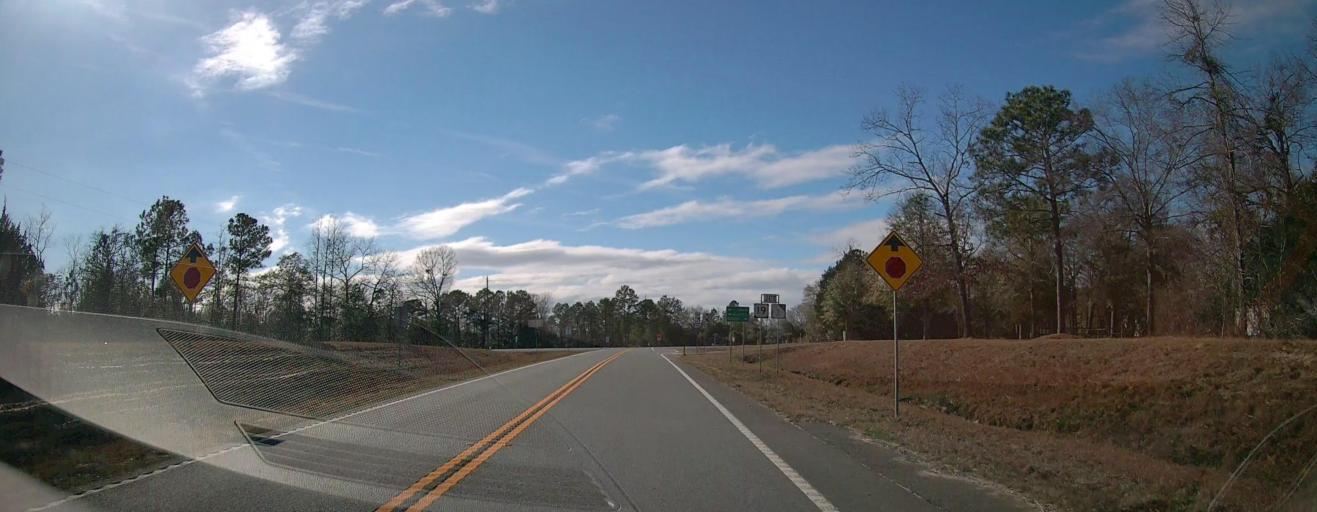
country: US
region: Georgia
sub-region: Taylor County
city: Butler
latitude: 32.4402
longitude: -84.2752
